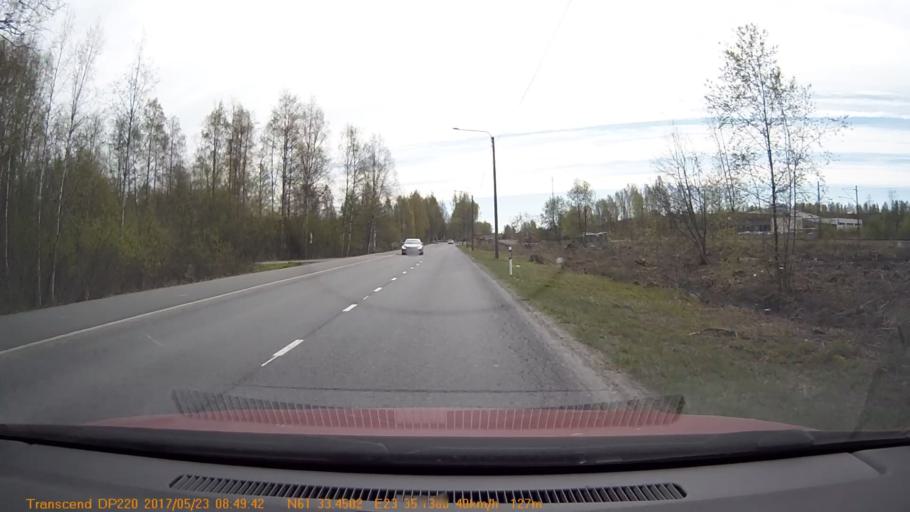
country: FI
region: Pirkanmaa
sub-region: Tampere
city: Yloejaervi
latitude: 61.5577
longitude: 23.5855
